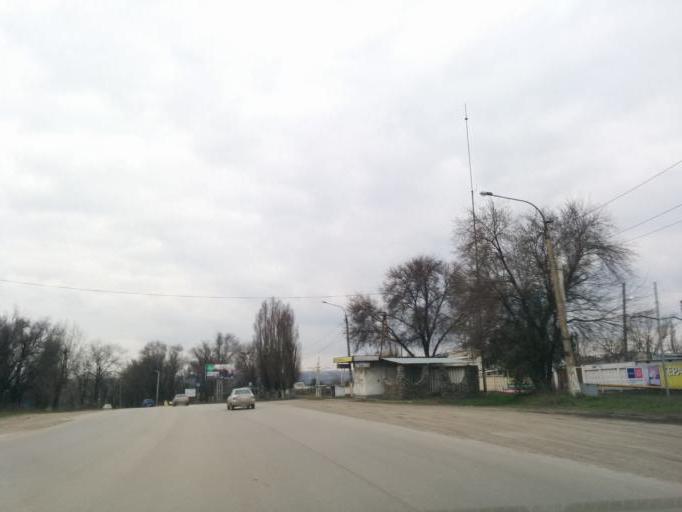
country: RU
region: Rostov
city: Novocherkassk
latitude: 47.4652
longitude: 40.0996
